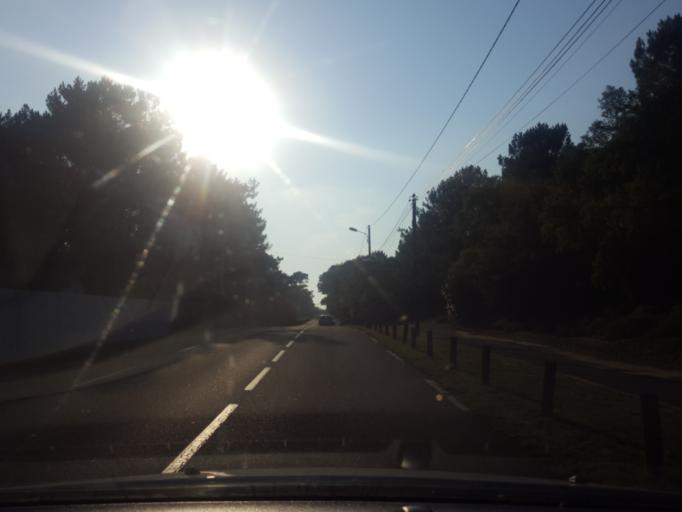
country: FR
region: Aquitaine
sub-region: Departement des Landes
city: Ondres
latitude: 43.5741
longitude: -1.4780
